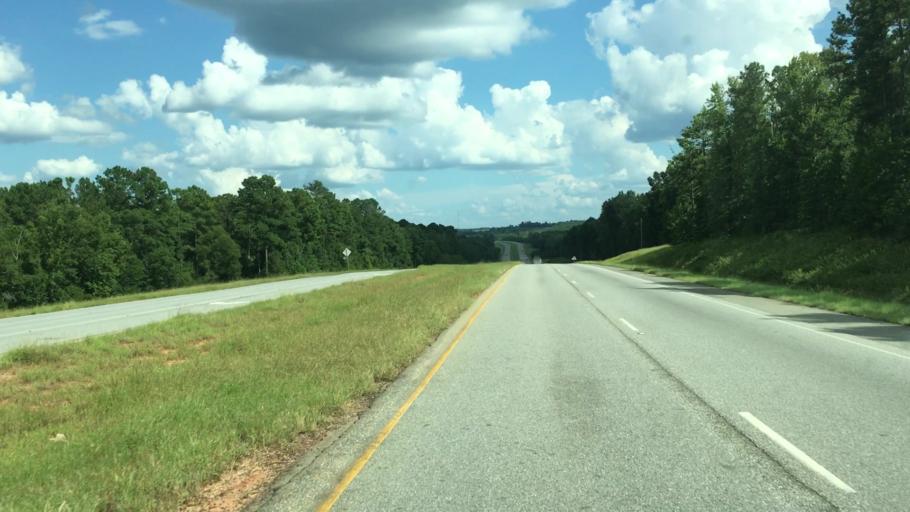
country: US
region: Georgia
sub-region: Wilkinson County
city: Irwinton
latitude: 32.7064
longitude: -83.1306
